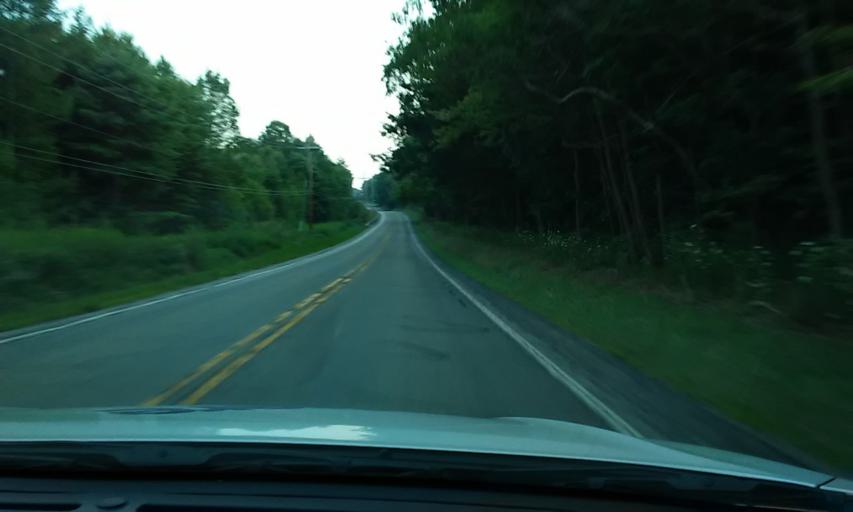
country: US
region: Pennsylvania
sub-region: Clarion County
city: Marianne
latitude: 41.2848
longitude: -79.3859
